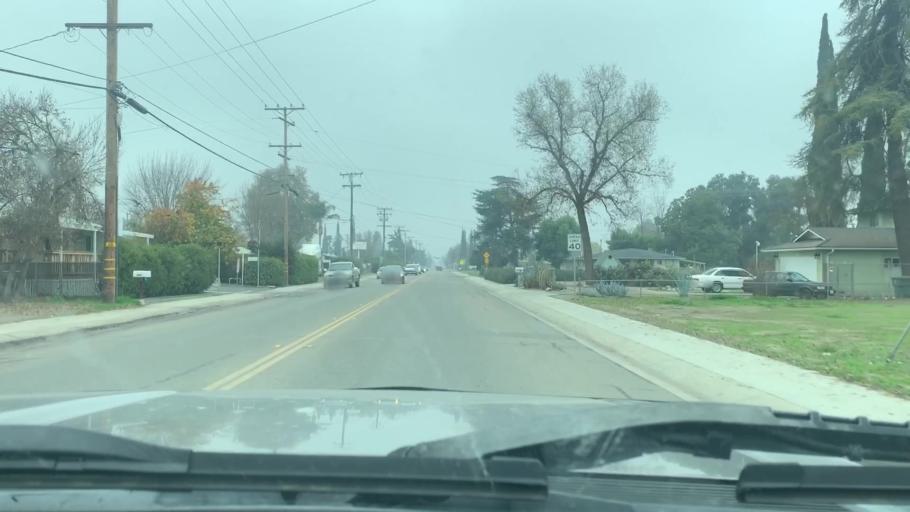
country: US
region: California
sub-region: Tulare County
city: Visalia
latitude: 36.3241
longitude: -119.3363
